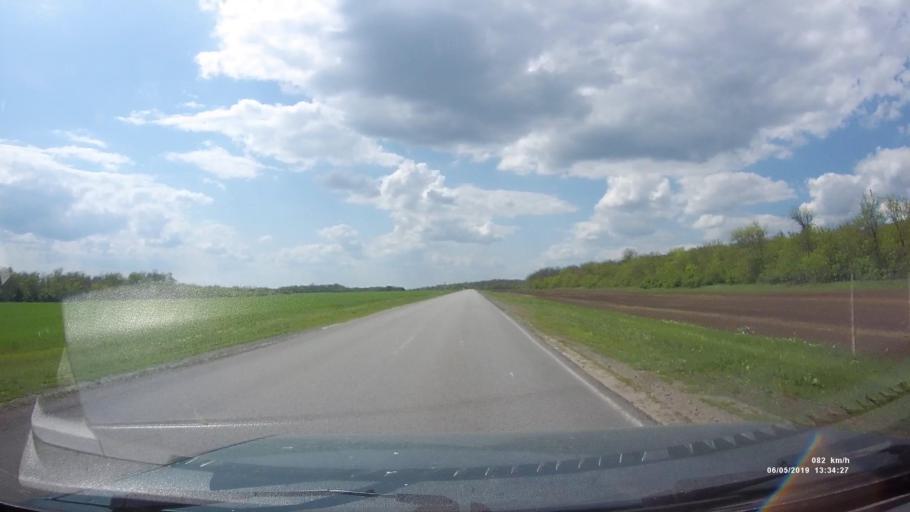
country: RU
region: Rostov
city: Ust'-Donetskiy
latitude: 47.6929
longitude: 40.7625
